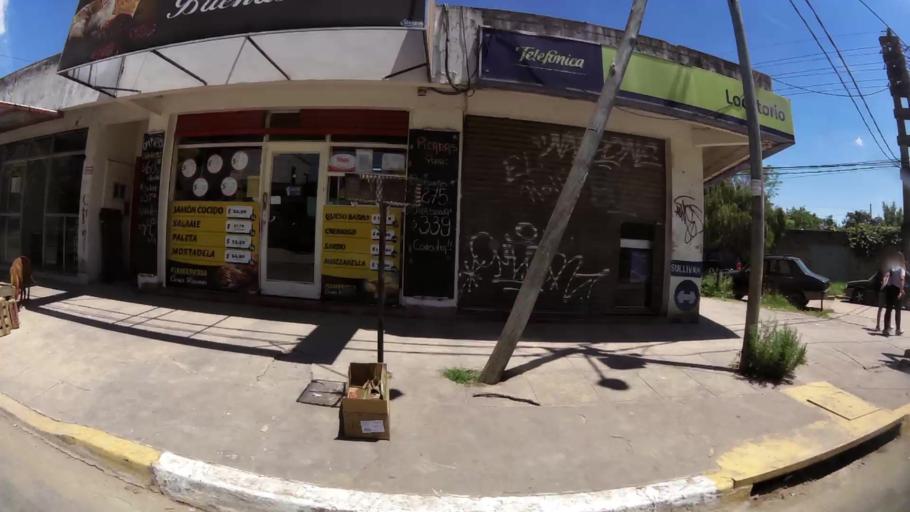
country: AR
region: Buenos Aires
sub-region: Partido de Merlo
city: Merlo
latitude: -34.6539
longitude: -58.7147
